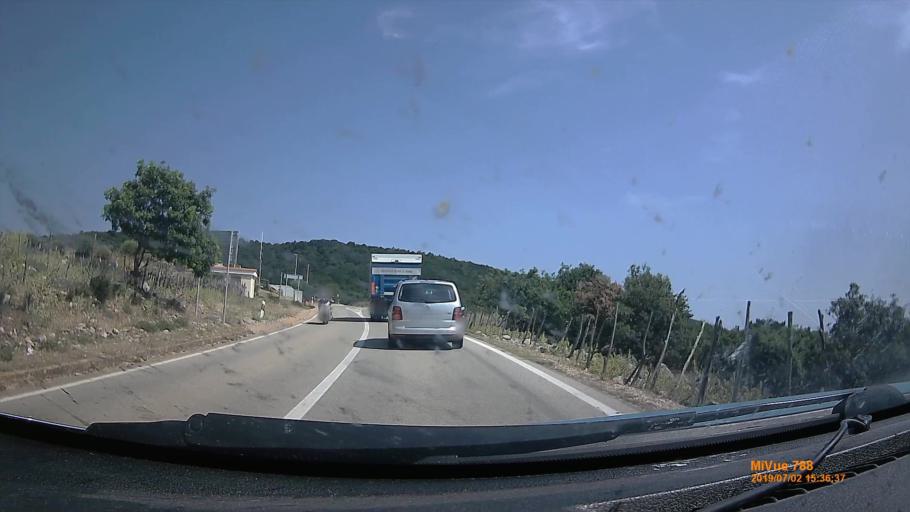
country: HR
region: Primorsko-Goranska
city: Cres
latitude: 44.9828
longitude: 14.4118
